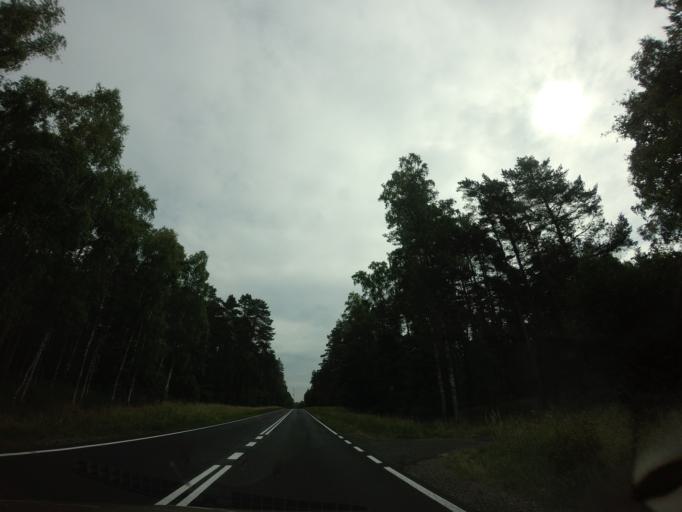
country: PL
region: West Pomeranian Voivodeship
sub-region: Powiat walecki
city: Miroslawiec
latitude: 53.3241
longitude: 16.0116
